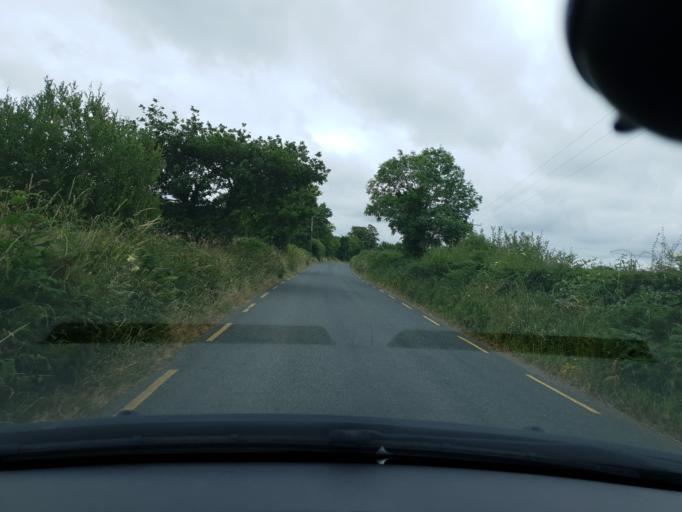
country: IE
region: Munster
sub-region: Ciarrai
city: Cill Airne
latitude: 52.1361
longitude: -9.5580
